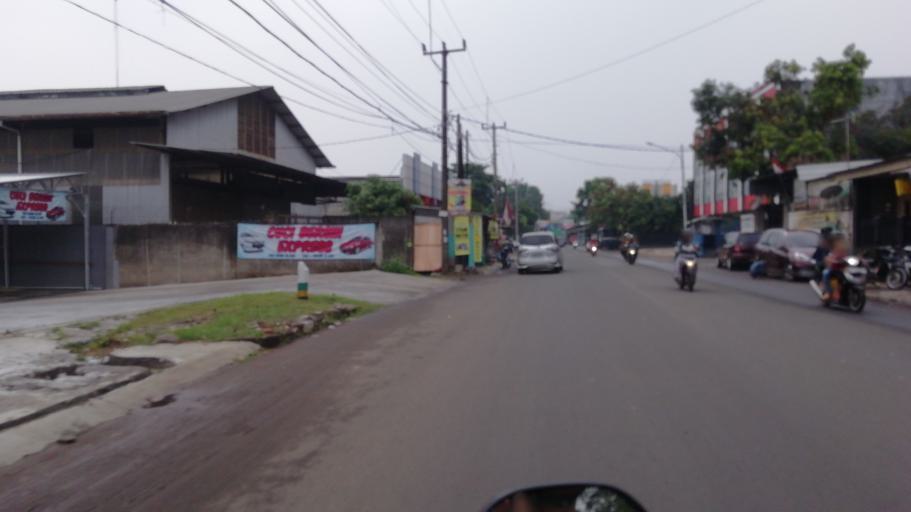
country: ID
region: West Java
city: Cibinong
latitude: -6.5304
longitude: 106.8100
